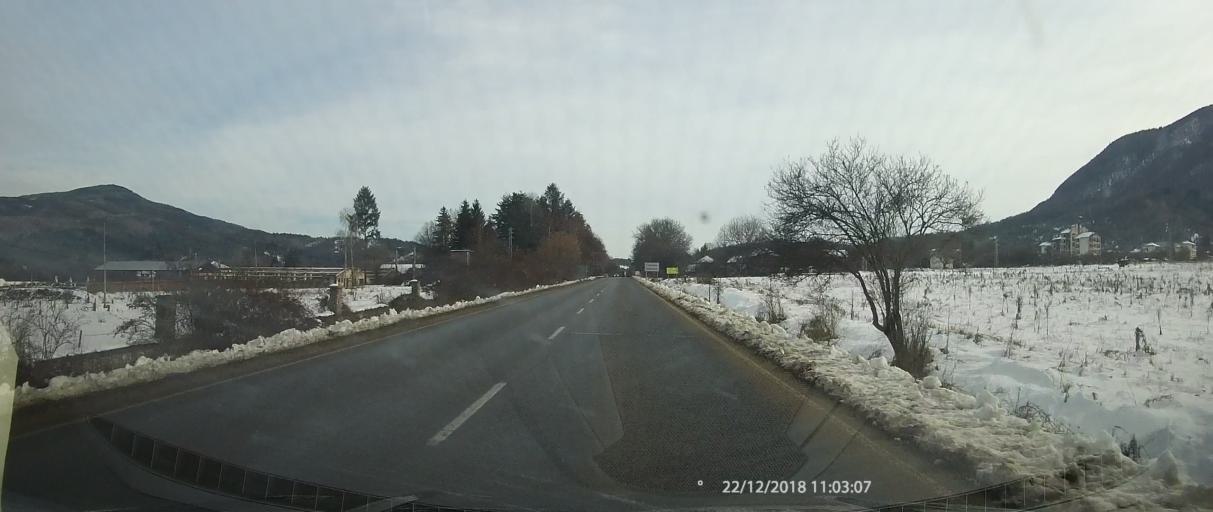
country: BG
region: Kyustendil
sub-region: Obshtina Kyustendil
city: Kyustendil
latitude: 42.2550
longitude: 22.5451
